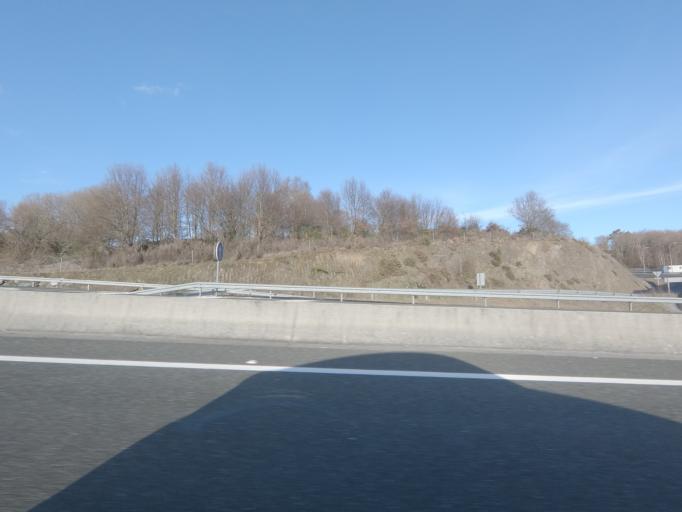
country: ES
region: Galicia
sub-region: Provincia de Pontevedra
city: Lalin
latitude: 42.6219
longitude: -8.0999
